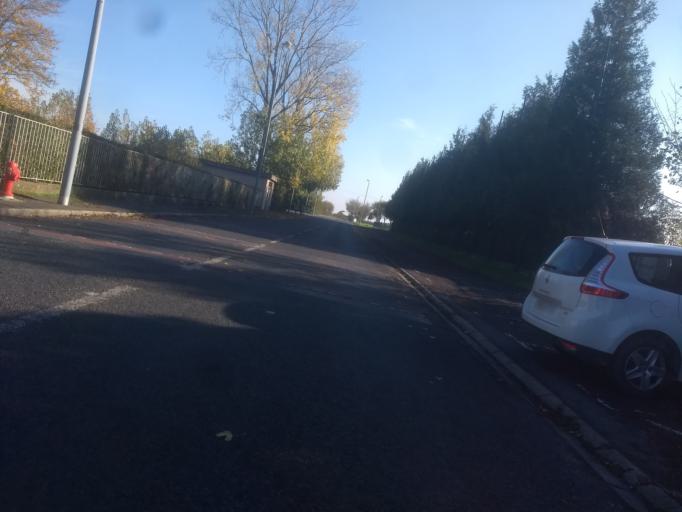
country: FR
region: Nord-Pas-de-Calais
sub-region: Departement du Pas-de-Calais
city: Beaurains
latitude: 50.2792
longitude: 2.7962
